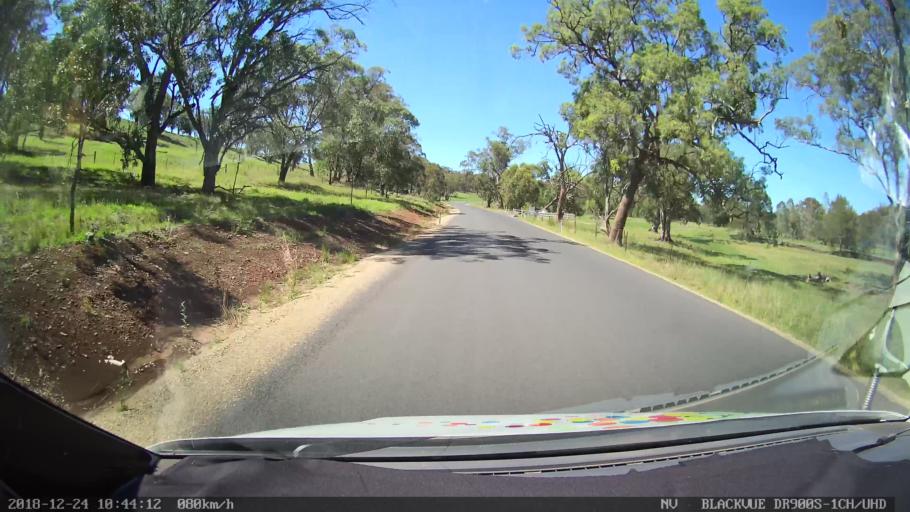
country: AU
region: New South Wales
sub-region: Upper Hunter Shire
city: Merriwa
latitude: -31.8904
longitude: 150.4439
